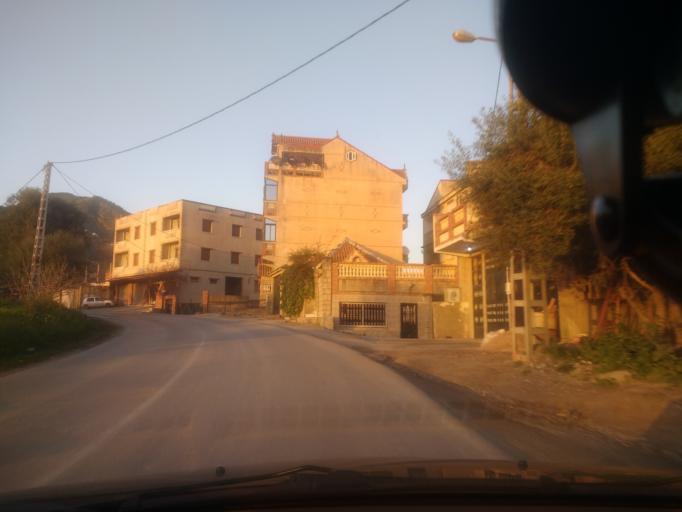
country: DZ
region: Boumerdes
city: Makouda
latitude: 36.7741
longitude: 4.0647
